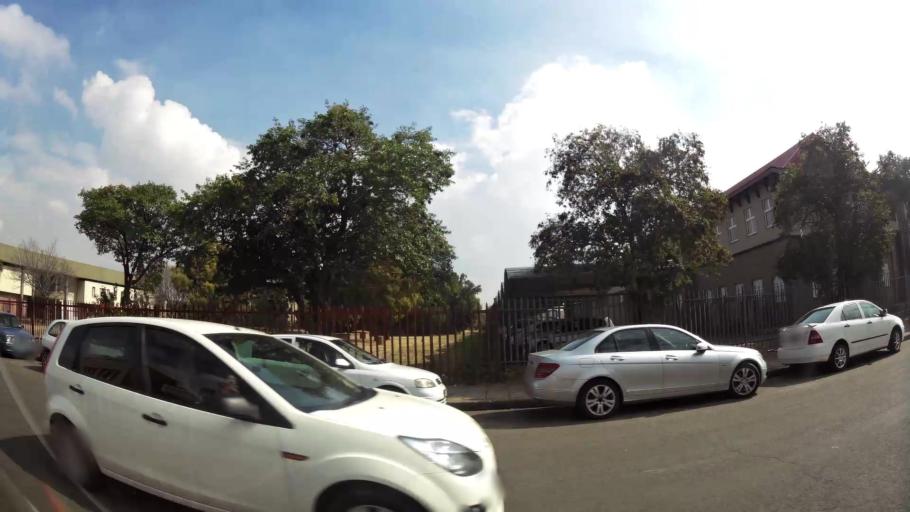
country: ZA
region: Gauteng
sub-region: Sedibeng District Municipality
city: Vereeniging
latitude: -26.6742
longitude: 27.9295
